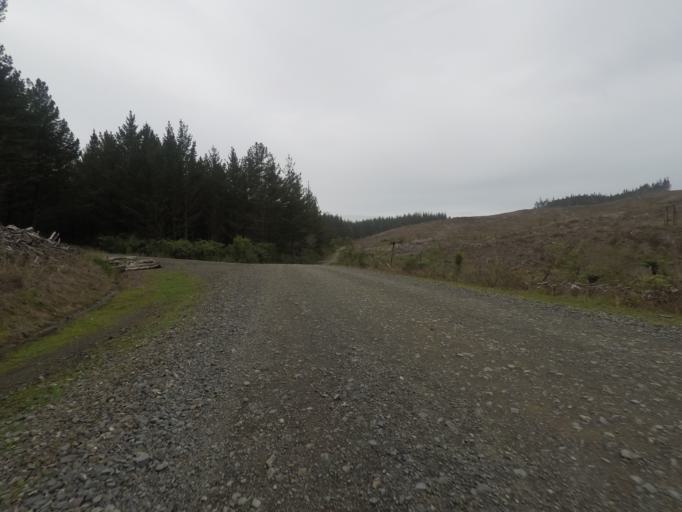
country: NZ
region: Auckland
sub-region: Auckland
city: Muriwai Beach
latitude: -36.7449
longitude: 174.5778
